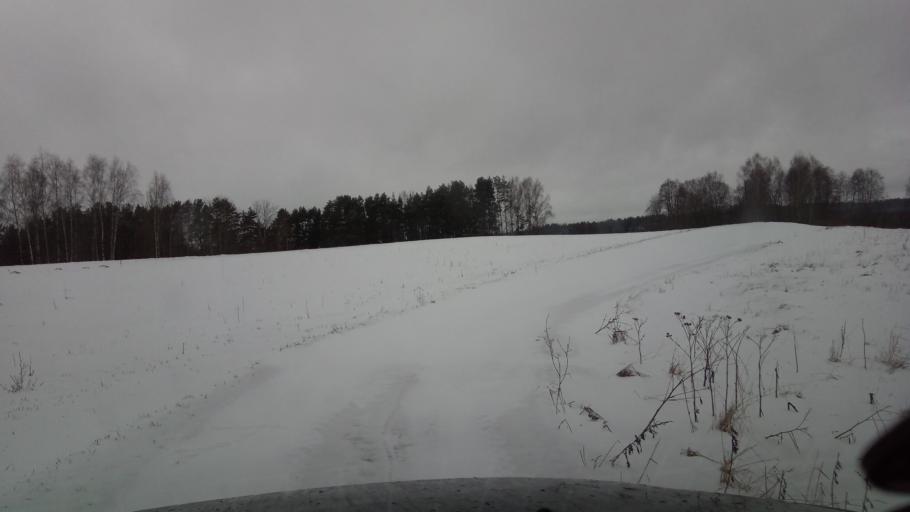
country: LT
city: Zarasai
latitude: 55.6381
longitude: 25.9805
